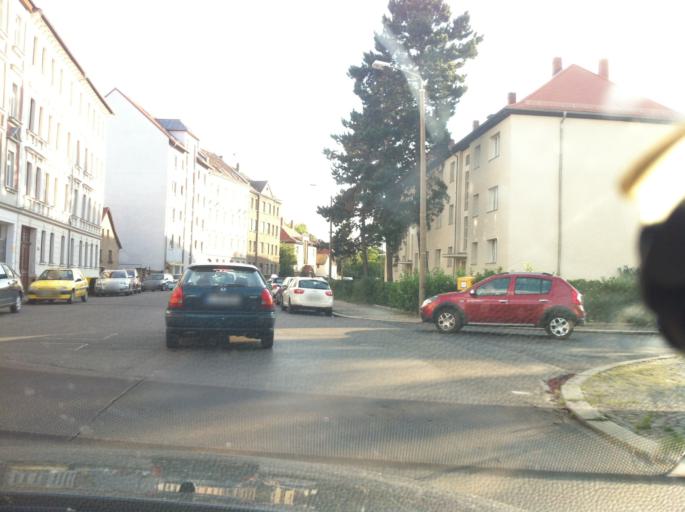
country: DE
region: Saxony
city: Markkleeberg
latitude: 51.2955
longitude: 12.3234
